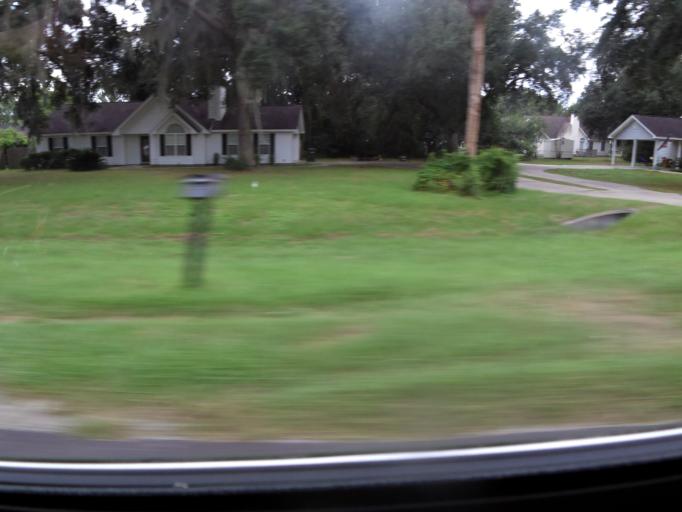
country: US
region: Georgia
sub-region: Glynn County
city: Dock Junction
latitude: 31.1505
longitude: -81.5900
